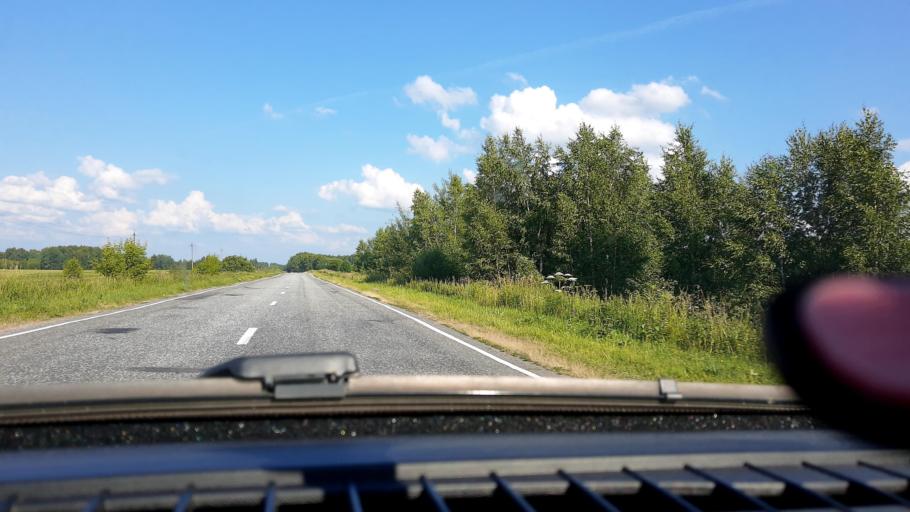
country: RU
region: Nizjnij Novgorod
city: Neklyudovo
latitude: 56.5198
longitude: 43.8938
